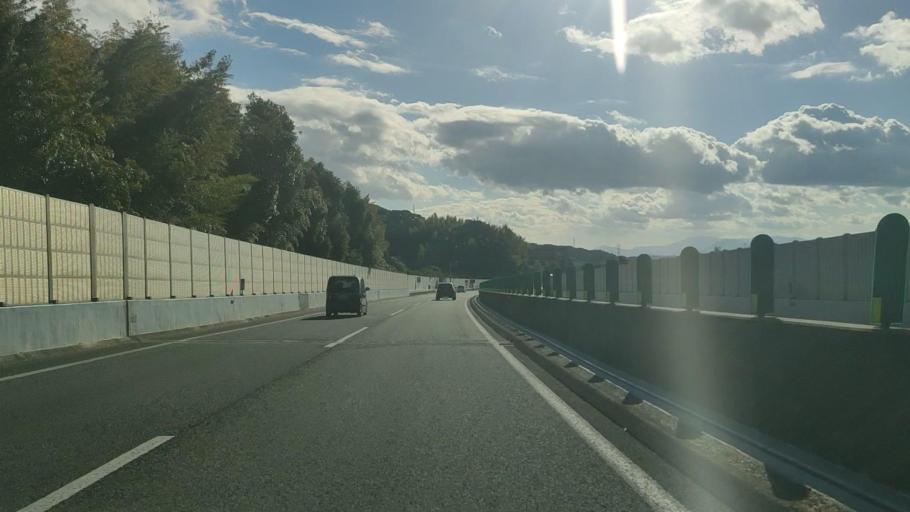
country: JP
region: Fukuoka
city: Nakama
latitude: 33.8304
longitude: 130.7655
